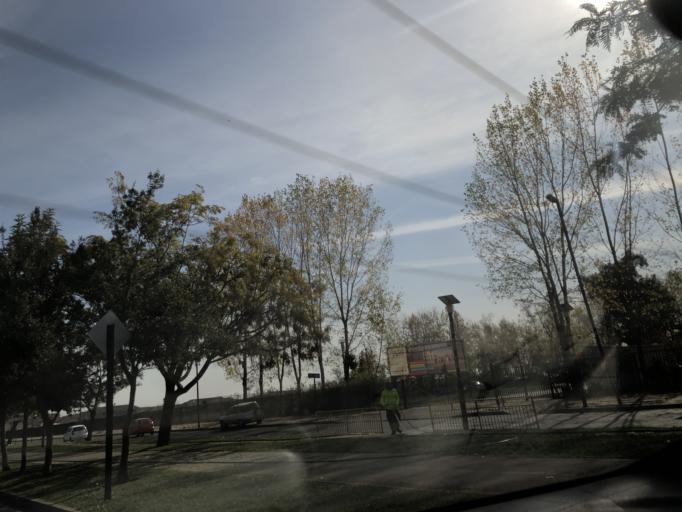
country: CL
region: Santiago Metropolitan
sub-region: Provincia de Cordillera
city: Puente Alto
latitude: -33.5957
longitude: -70.5816
